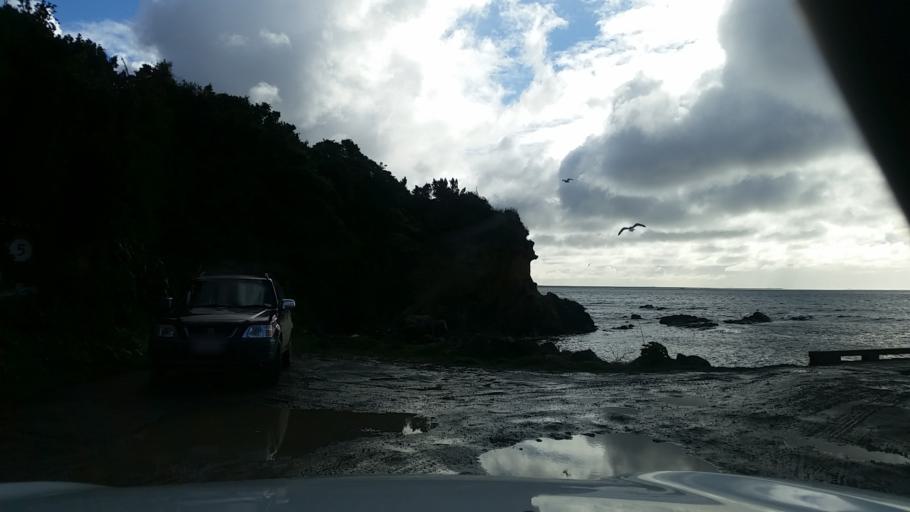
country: NZ
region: Chatham Islands
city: Waitangi
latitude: -44.0248
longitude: -176.3678
